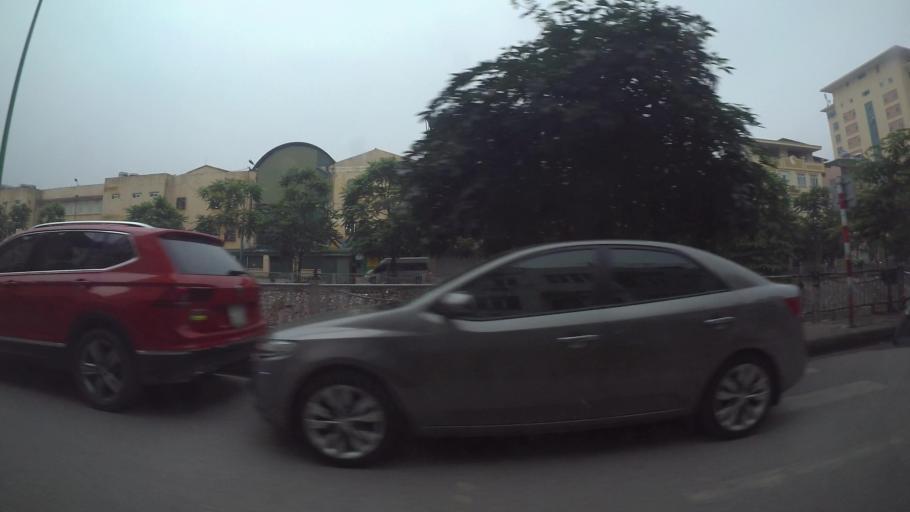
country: VN
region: Ha Noi
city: Hai BaTrung
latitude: 20.9896
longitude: 105.8371
